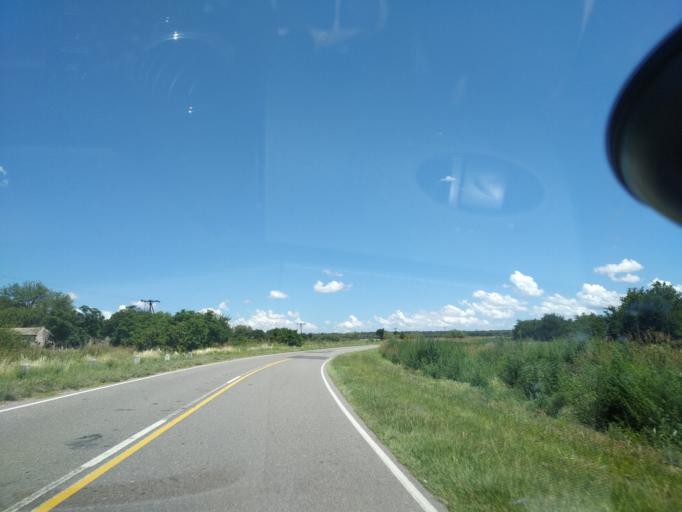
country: AR
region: Cordoba
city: Salsacate
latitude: -31.4183
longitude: -65.0946
